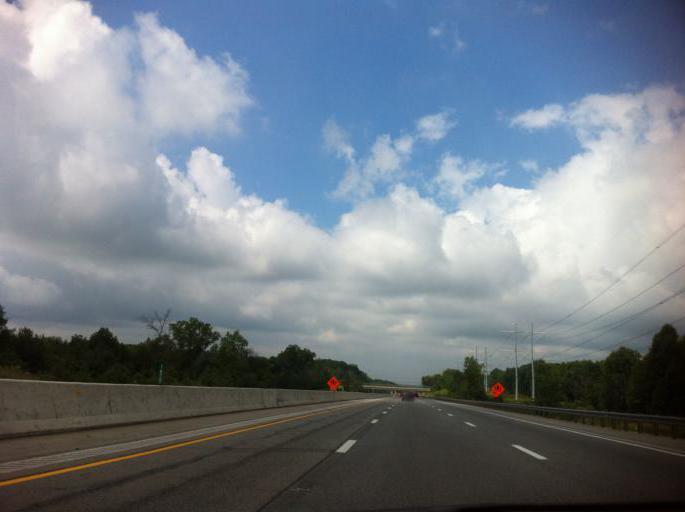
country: US
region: Ohio
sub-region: Cuyahoga County
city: North Royalton
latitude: 41.3032
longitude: -81.7174
